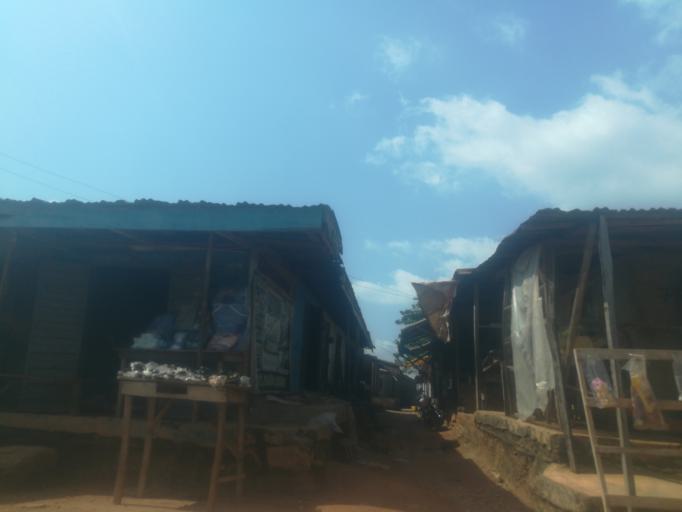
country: NG
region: Oyo
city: Moniya
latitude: 7.5025
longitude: 3.9144
